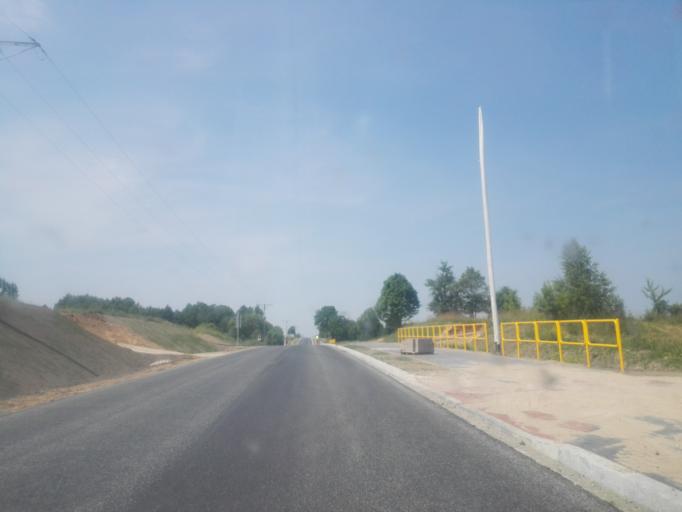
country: PL
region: Podlasie
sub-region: Suwalki
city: Suwalki
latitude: 54.0847
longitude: 23.0060
